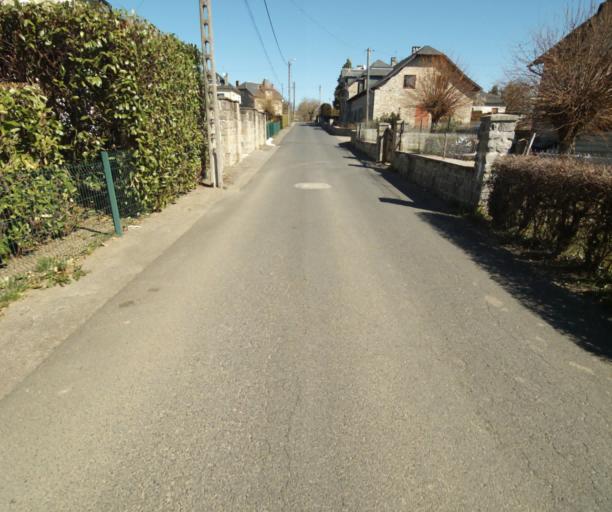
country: FR
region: Limousin
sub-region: Departement de la Correze
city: Chamboulive
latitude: 45.4291
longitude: 1.7085
